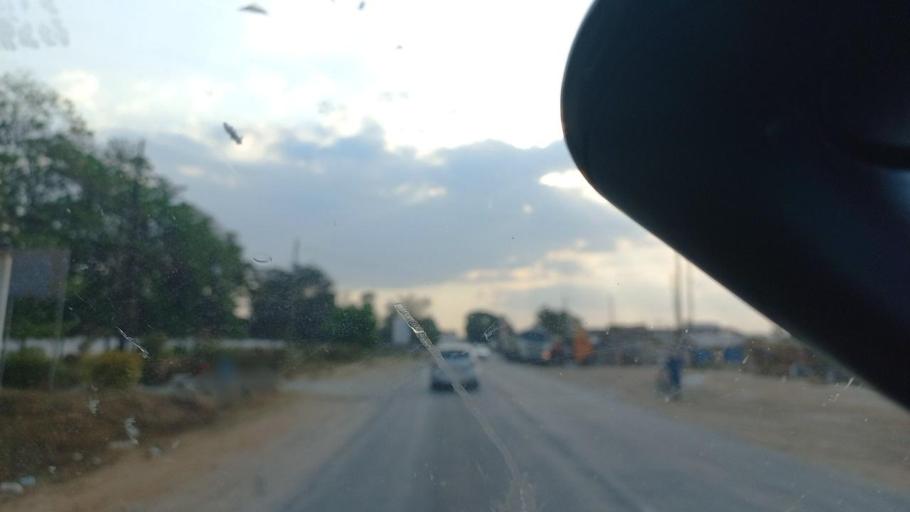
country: ZM
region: Lusaka
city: Lusaka
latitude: -15.3697
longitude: 28.4057
